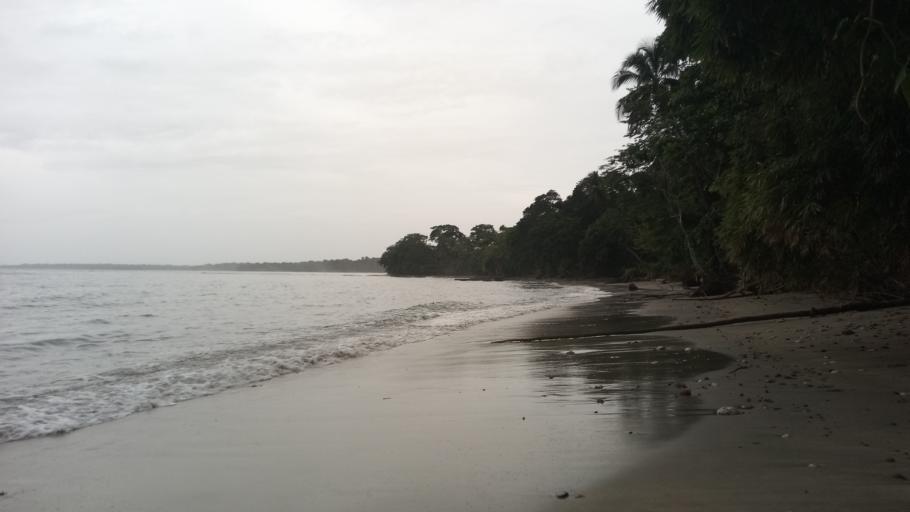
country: CR
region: Limon
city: Sixaola
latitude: 9.6283
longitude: -82.6199
